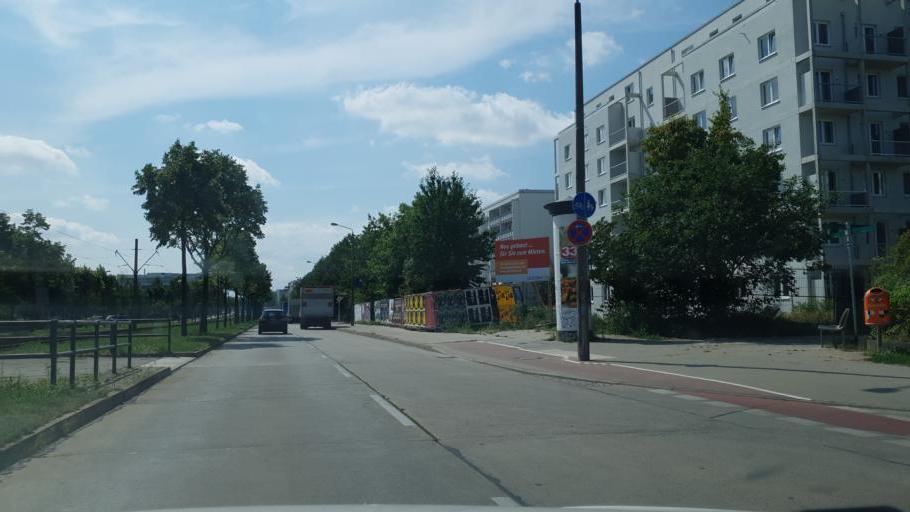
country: DE
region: Berlin
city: Hellersdorf
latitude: 52.5427
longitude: 13.6034
